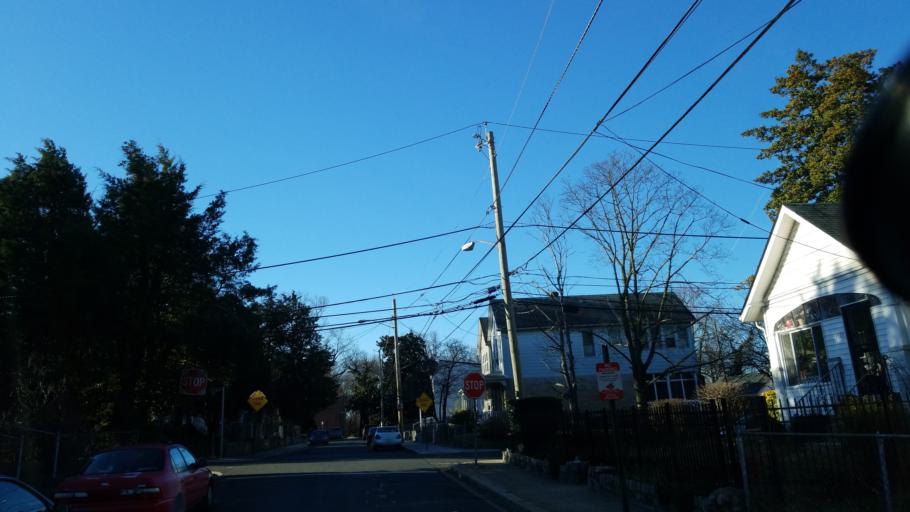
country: US
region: Maryland
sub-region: Prince George's County
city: Glassmanor
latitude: 38.8402
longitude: -77.0058
